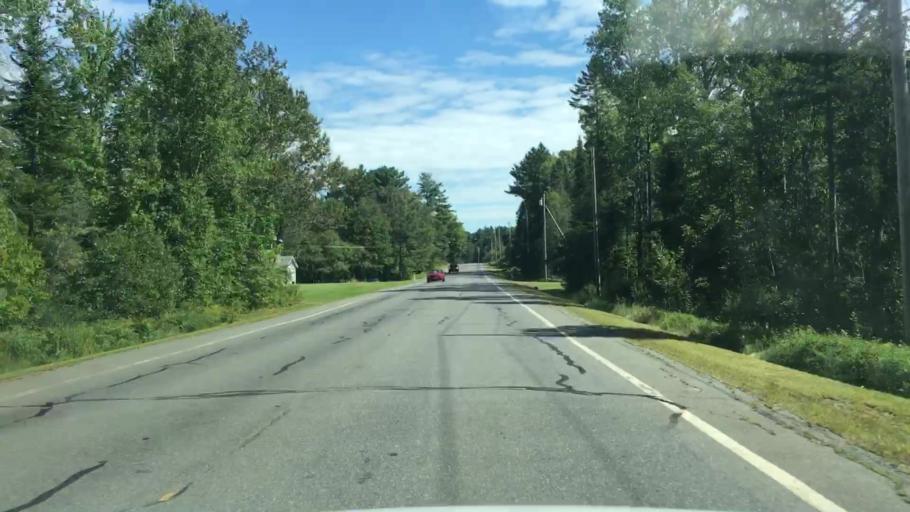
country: US
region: Maine
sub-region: Penobscot County
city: Garland
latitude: 45.0900
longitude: -69.2188
